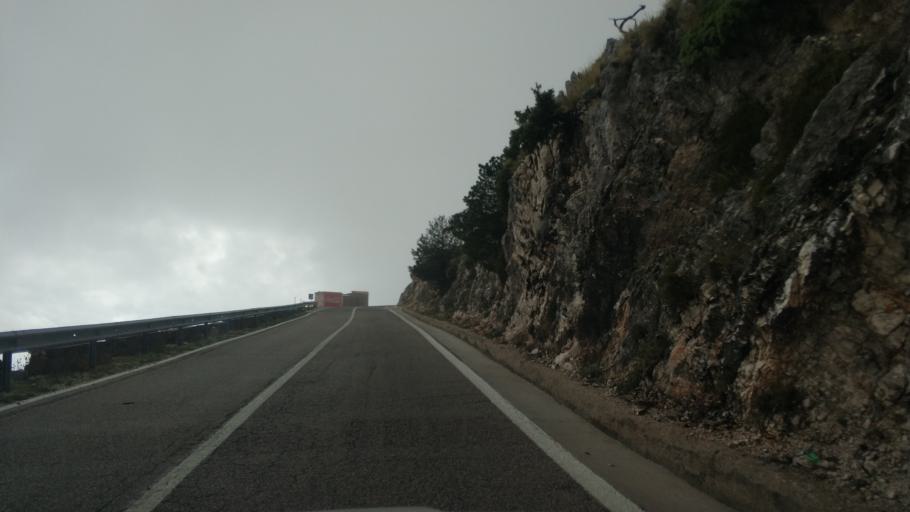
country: AL
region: Vlore
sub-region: Rrethi i Vlores
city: Vranisht
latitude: 40.1889
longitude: 19.6004
